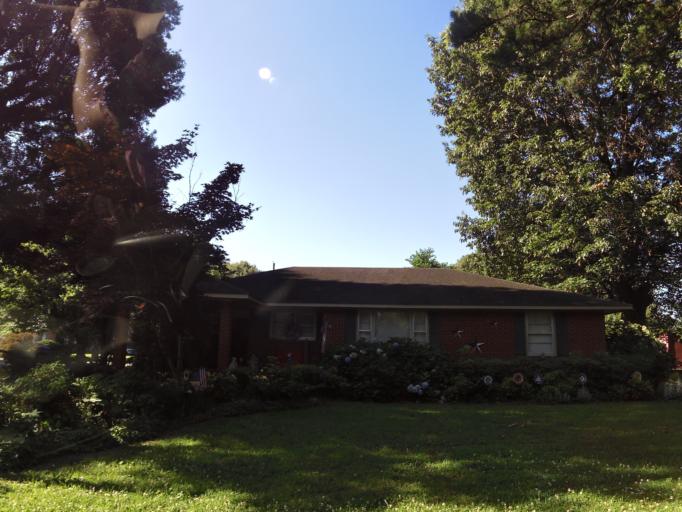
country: US
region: Arkansas
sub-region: Clay County
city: Corning
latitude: 36.4077
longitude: -90.5912
